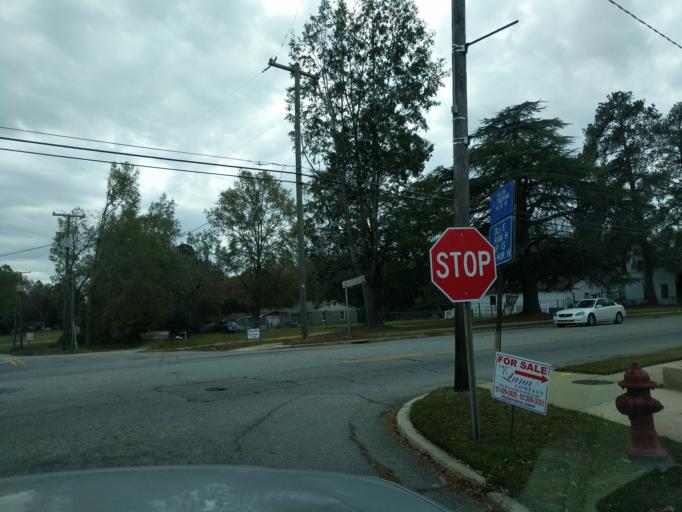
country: US
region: South Carolina
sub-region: Lexington County
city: Batesburg
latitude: 33.9042
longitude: -81.5478
